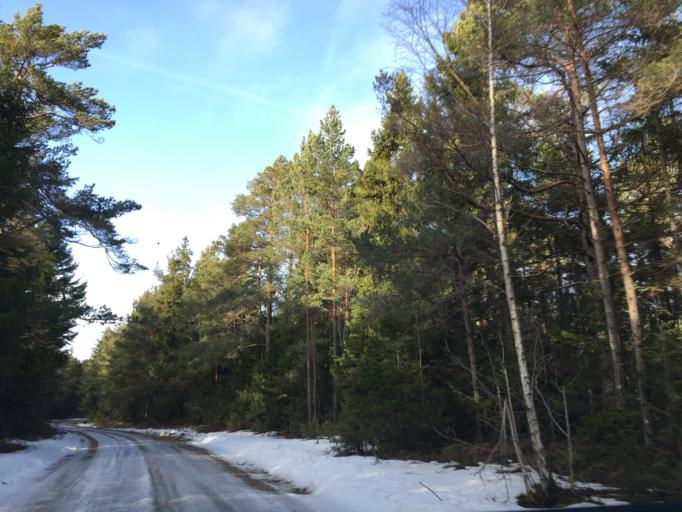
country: EE
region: Saare
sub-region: Kuressaare linn
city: Kuressaare
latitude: 58.4740
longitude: 21.9578
